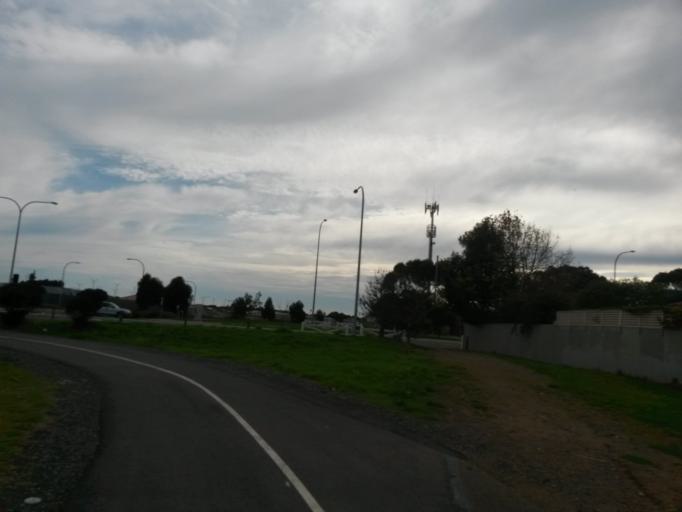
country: AU
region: South Australia
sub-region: Onkaparinga
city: Moana
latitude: -35.1919
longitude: 138.4840
